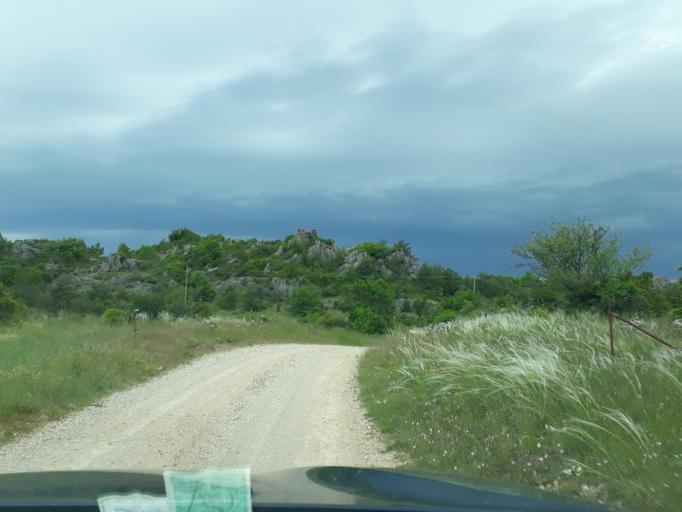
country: FR
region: Languedoc-Roussillon
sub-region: Departement de l'Herault
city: Lodeve
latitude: 43.8157
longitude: 3.2704
